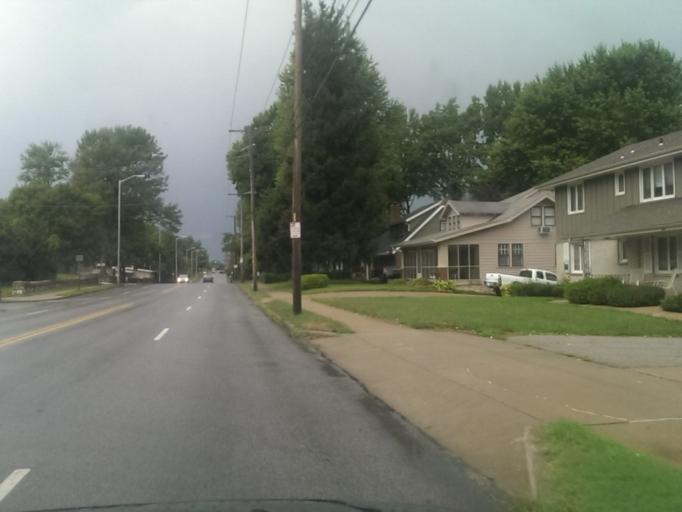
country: US
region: Kansas
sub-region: Johnson County
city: Leawood
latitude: 38.9920
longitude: -94.5856
